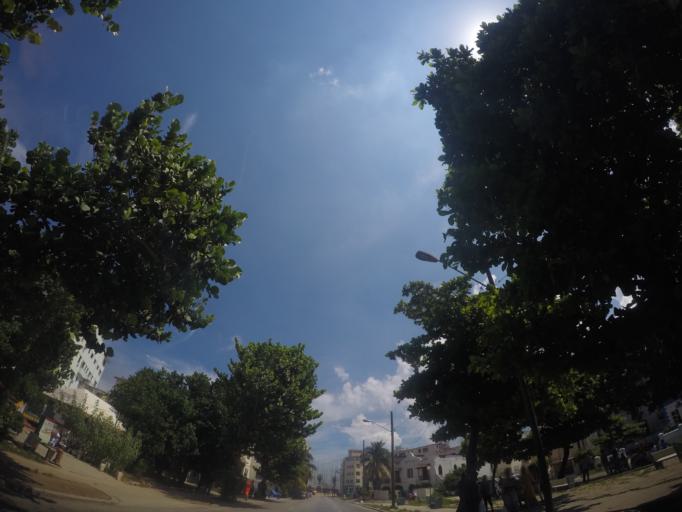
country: CU
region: La Habana
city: Havana
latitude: 23.1452
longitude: -82.3897
